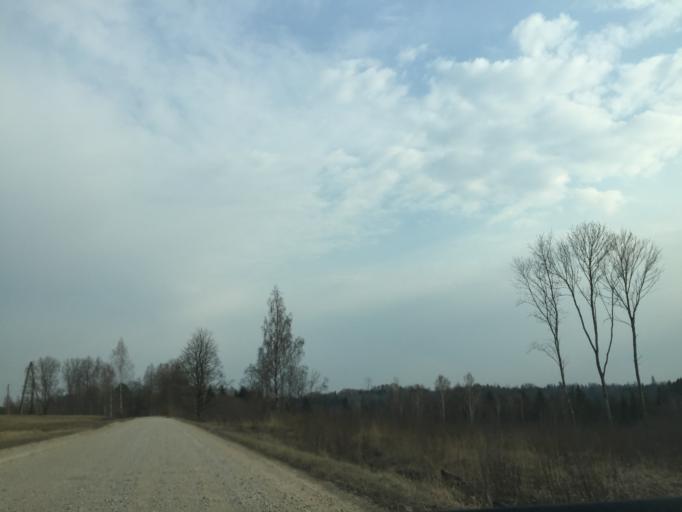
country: LV
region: Raunas
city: Rauna
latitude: 57.1569
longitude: 25.5768
